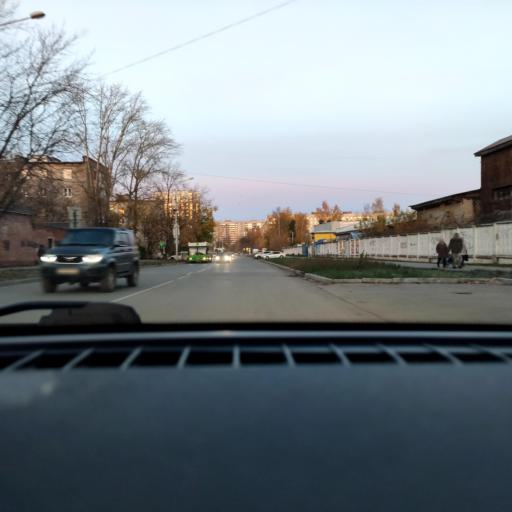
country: RU
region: Perm
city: Perm
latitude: 57.9643
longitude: 56.2235
